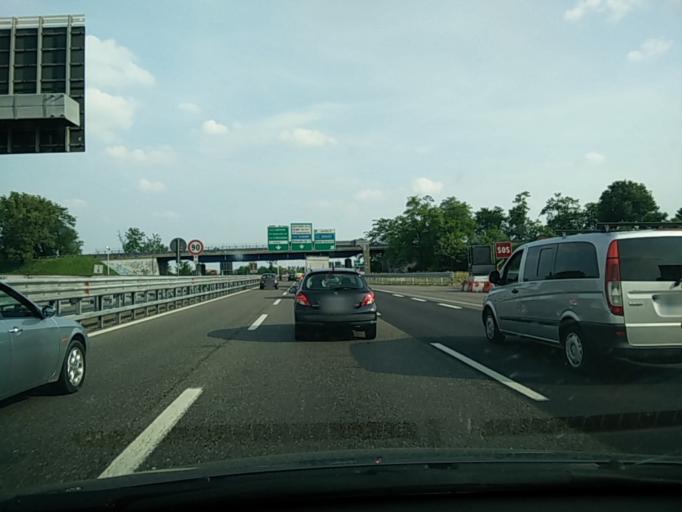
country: IT
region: Lombardy
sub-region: Citta metropolitana di Milano
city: Figino
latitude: 45.5036
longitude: 9.0655
